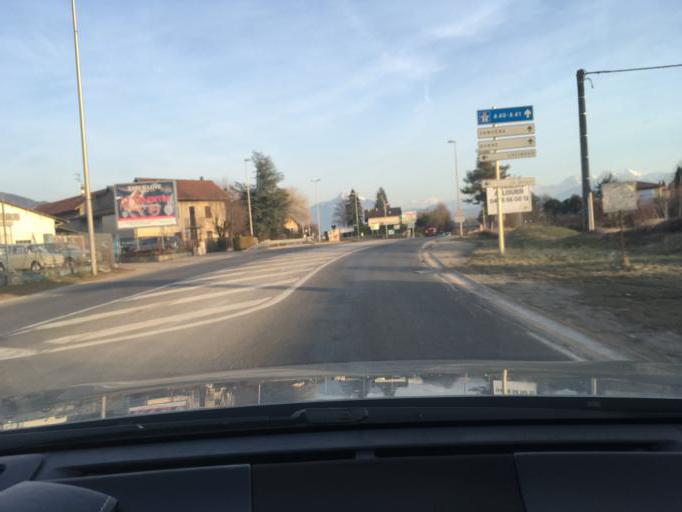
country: FR
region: Rhone-Alpes
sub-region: Departement de la Haute-Savoie
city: Cranves-Sales
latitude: 46.1816
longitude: 6.2853
